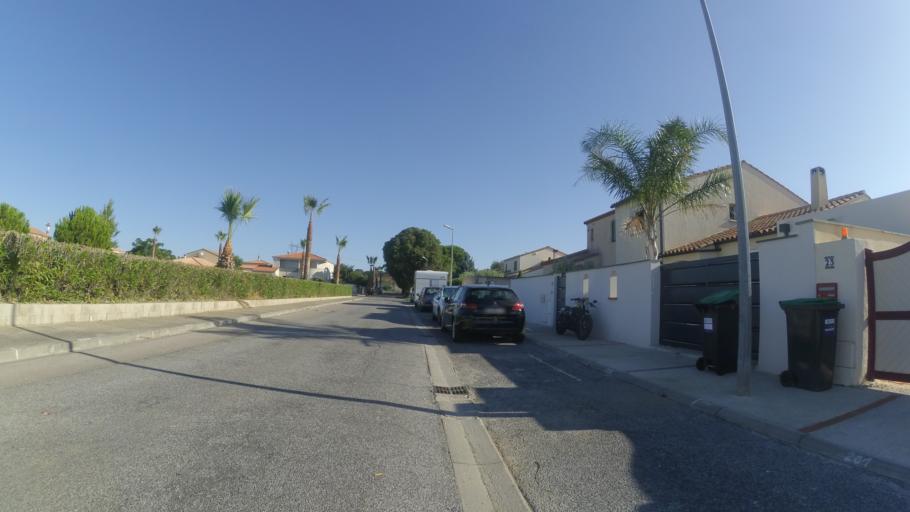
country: FR
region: Languedoc-Roussillon
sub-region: Departement des Pyrenees-Orientales
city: Baho
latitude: 42.7050
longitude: 2.8222
